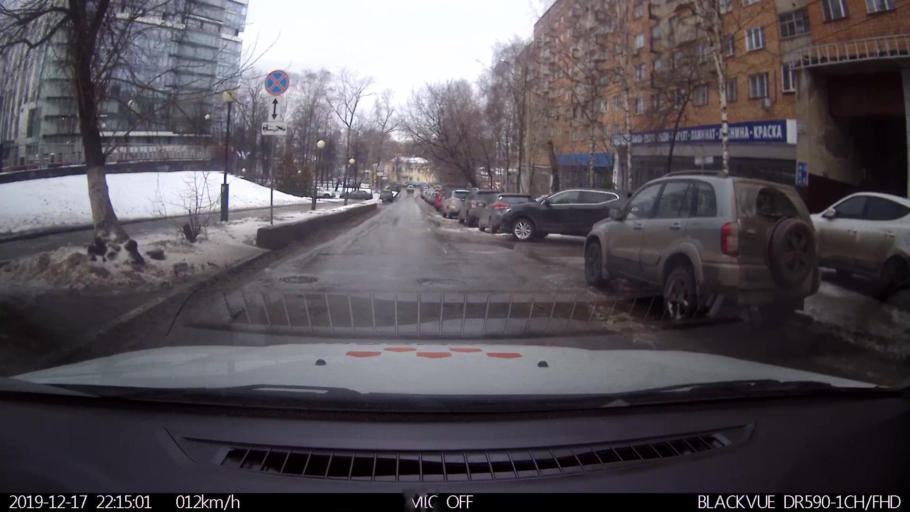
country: RU
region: Nizjnij Novgorod
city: Nizhniy Novgorod
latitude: 56.3162
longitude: 44.0029
